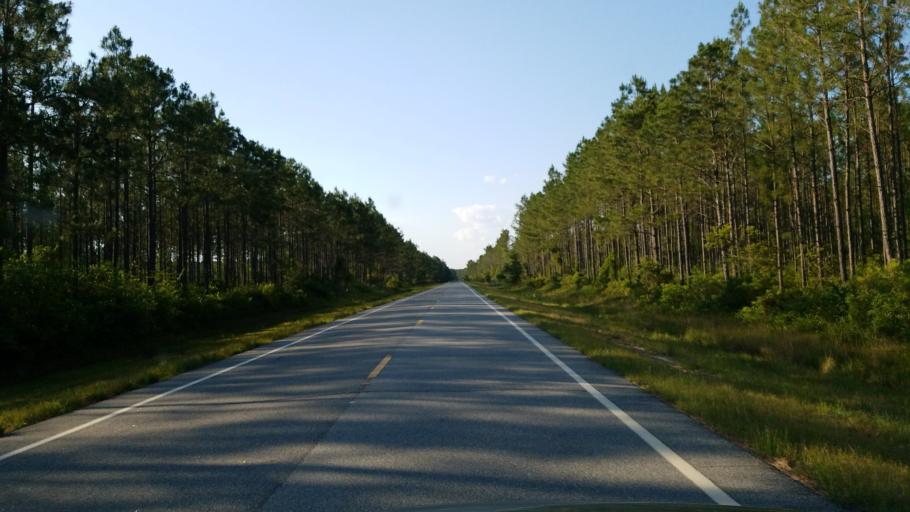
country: US
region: Georgia
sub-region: Lanier County
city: Lakeland
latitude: 30.8742
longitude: -83.0525
